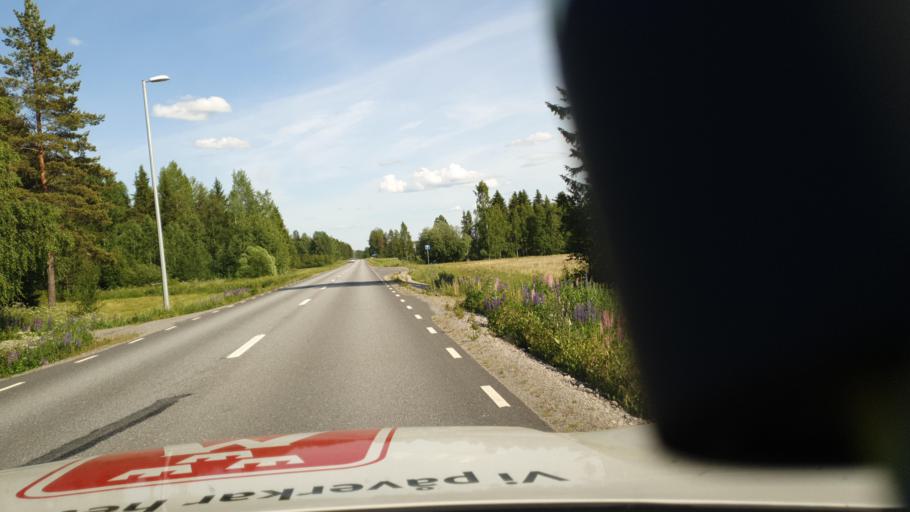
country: SE
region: Vaesterbotten
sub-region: Skelleftea Kommun
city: Forsbacka
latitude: 64.7027
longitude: 20.4524
